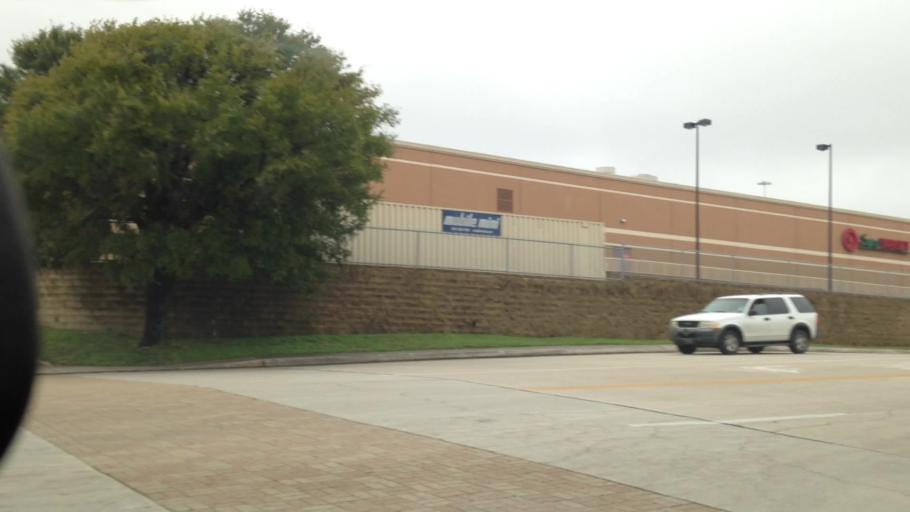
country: US
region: Texas
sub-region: Bexar County
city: Balcones Heights
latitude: 29.4943
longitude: -98.5494
